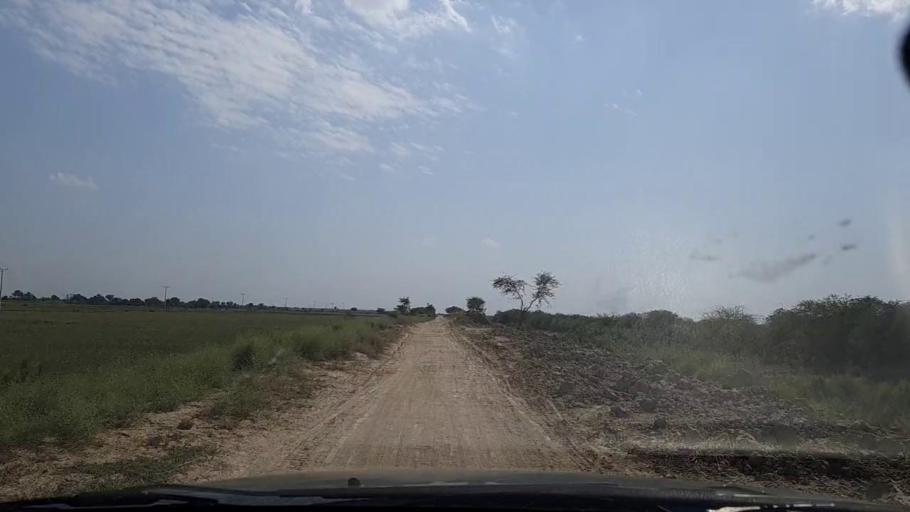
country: PK
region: Sindh
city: Mirpur Batoro
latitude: 24.5864
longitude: 68.1969
